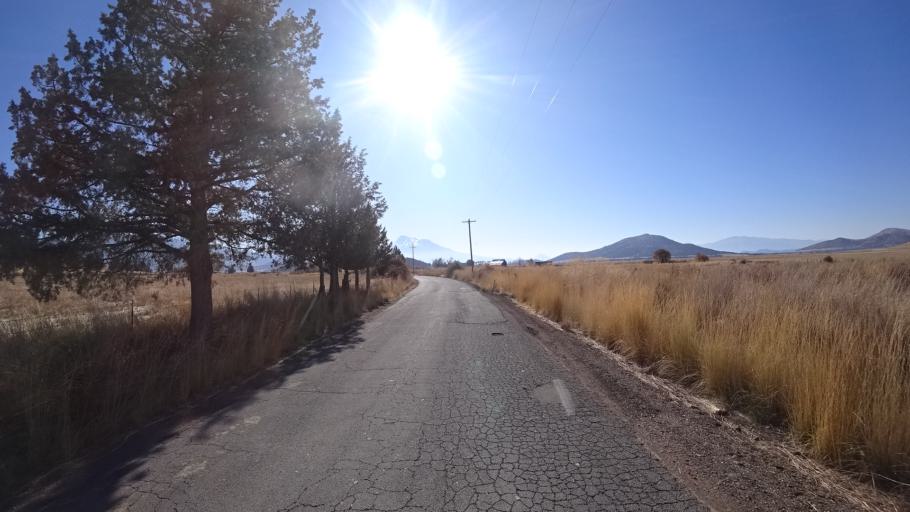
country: US
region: California
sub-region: Siskiyou County
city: Montague
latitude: 41.7038
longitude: -122.3785
